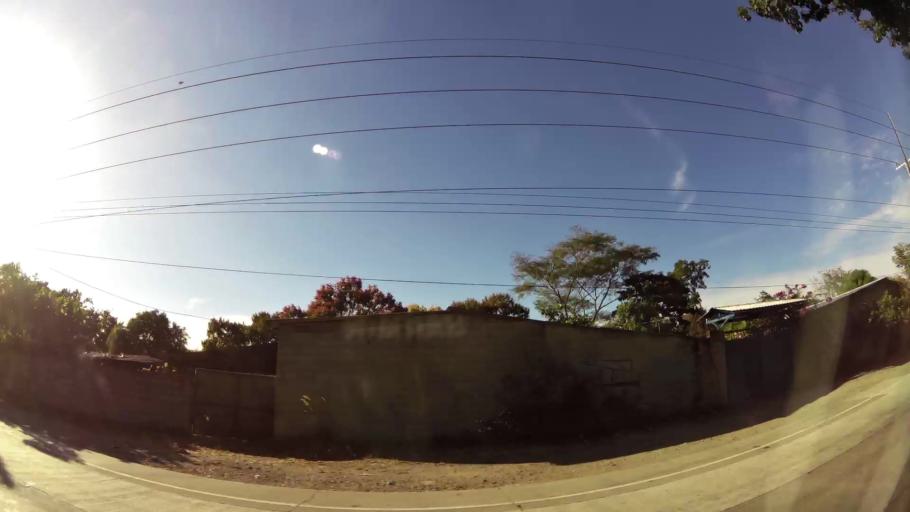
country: SV
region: Santa Ana
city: Metapan
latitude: 14.2454
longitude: -89.4704
